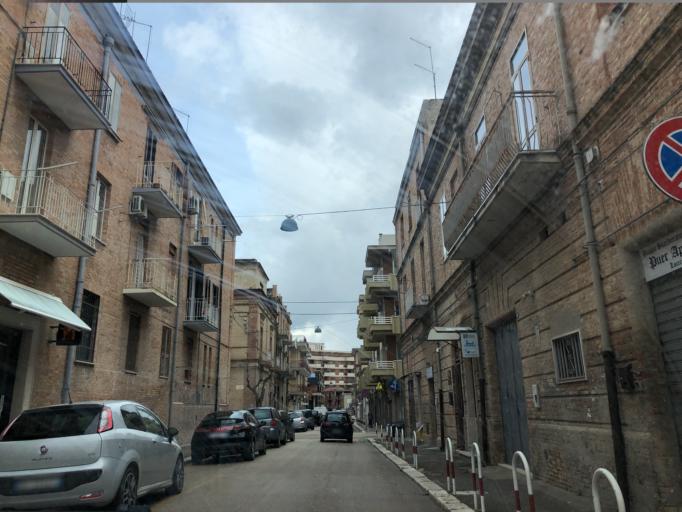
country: IT
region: Apulia
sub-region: Provincia di Foggia
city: Lucera
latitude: 41.5072
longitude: 15.3302
